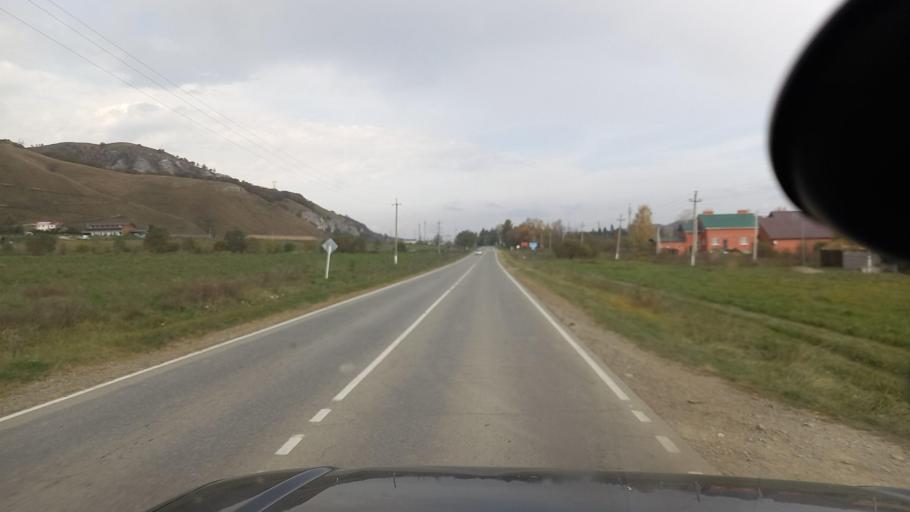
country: RU
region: Krasnodarskiy
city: Psebay
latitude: 44.1438
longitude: 40.8243
